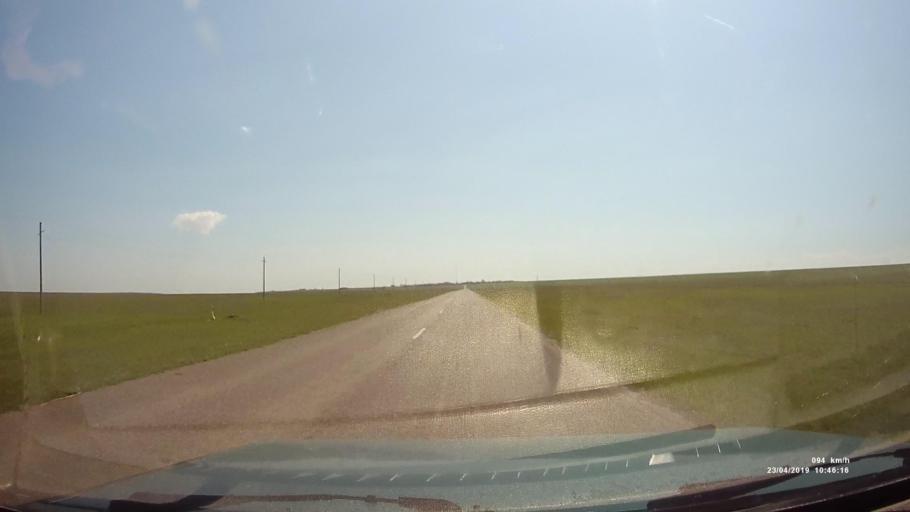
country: RU
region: Kalmykiya
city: Yashalta
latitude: 46.4444
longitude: 42.6884
